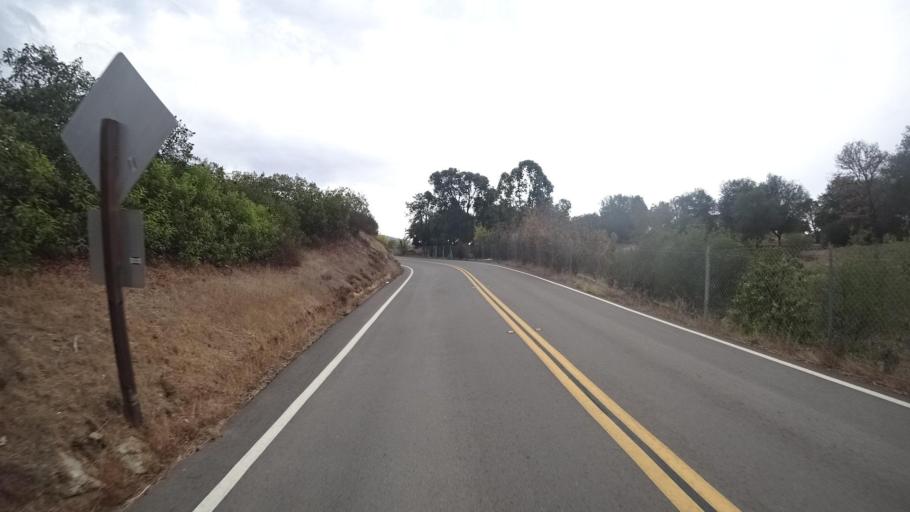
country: US
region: California
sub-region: San Diego County
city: San Pasqual
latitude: 33.0353
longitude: -116.9738
